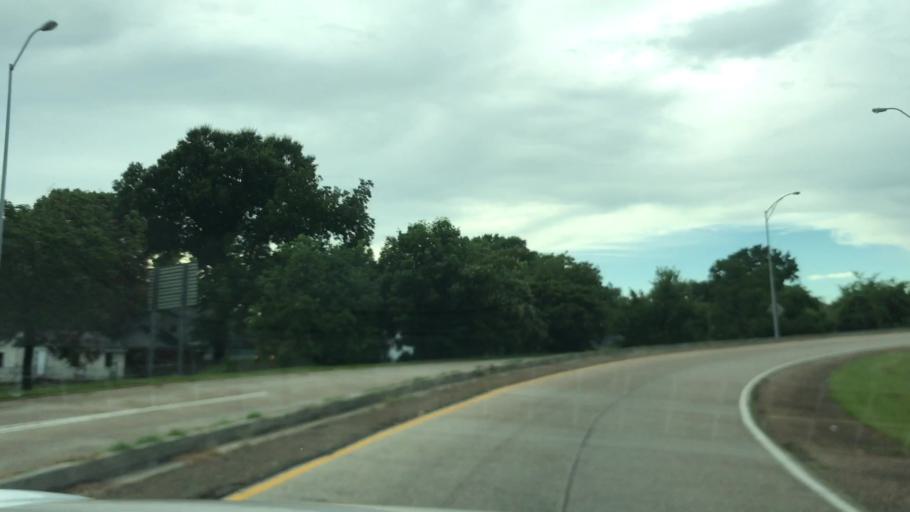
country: US
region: Louisiana
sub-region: East Baton Rouge Parish
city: Brownsfield
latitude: 30.5217
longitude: -91.1633
